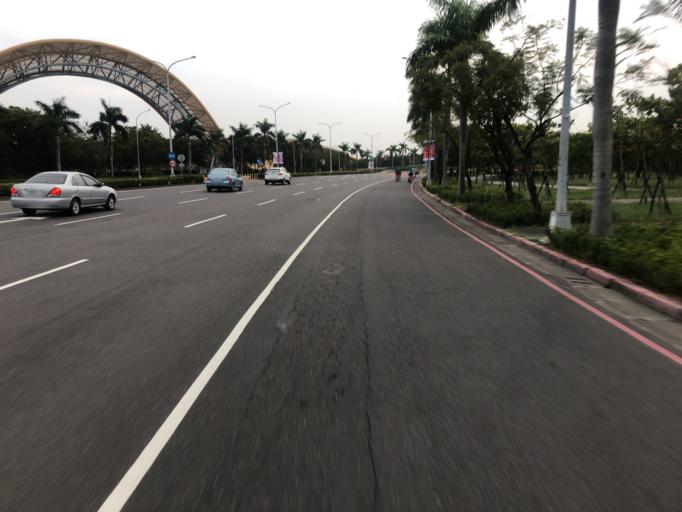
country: TW
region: Taiwan
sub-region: Tainan
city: Tainan
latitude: 23.0889
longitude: 120.2827
